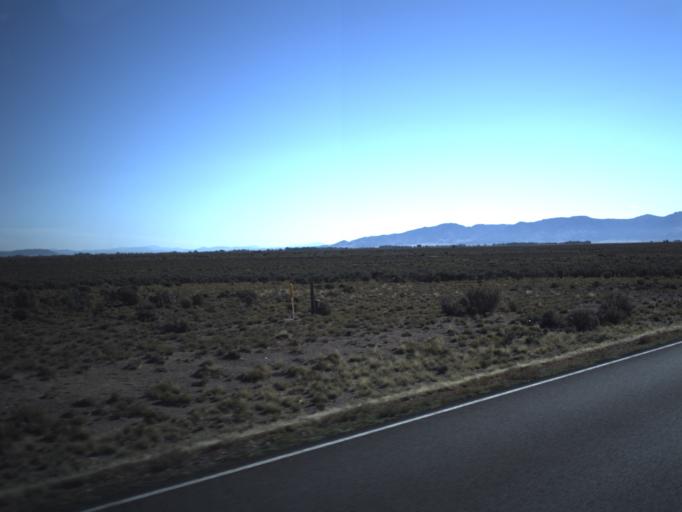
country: US
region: Utah
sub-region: Washington County
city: Enterprise
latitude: 37.7313
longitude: -113.7171
